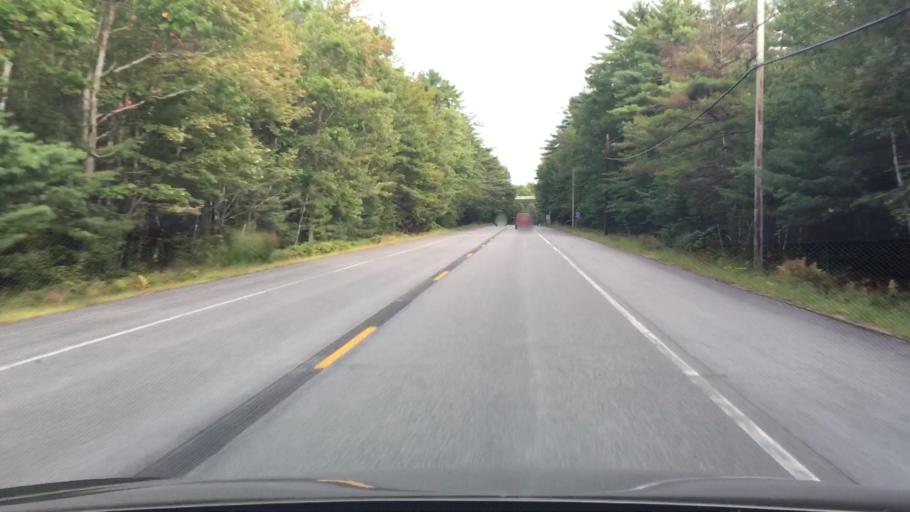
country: US
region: Maine
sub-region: Cumberland County
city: Bridgton
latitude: 44.0638
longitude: -70.7401
